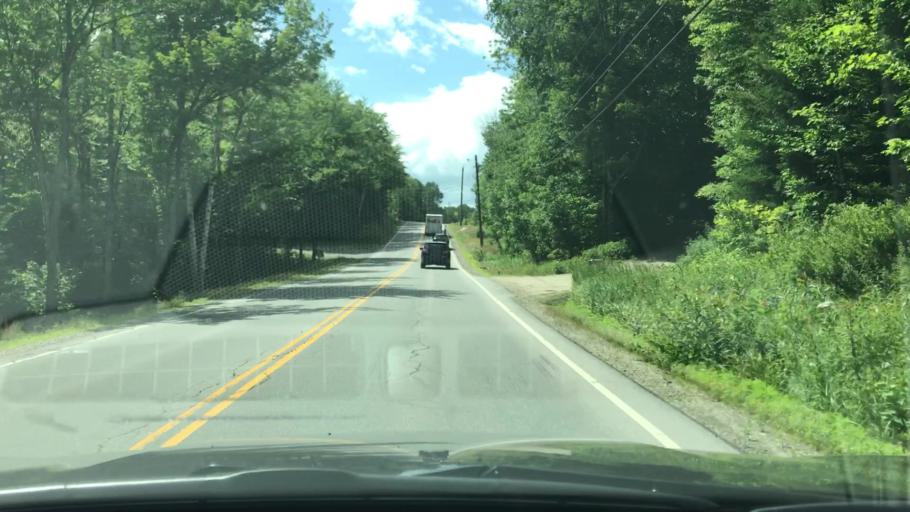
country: US
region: New Hampshire
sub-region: Coos County
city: Jefferson
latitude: 44.3621
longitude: -71.3824
